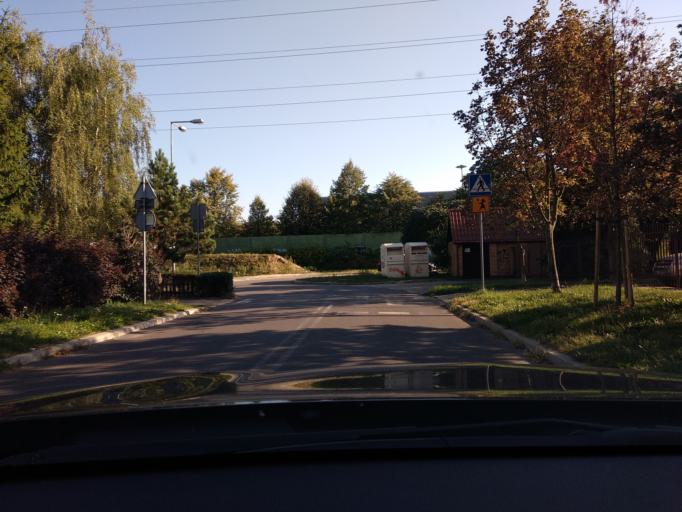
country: PL
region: Masovian Voivodeship
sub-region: Warszawa
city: Ursynow
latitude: 52.1281
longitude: 21.0558
